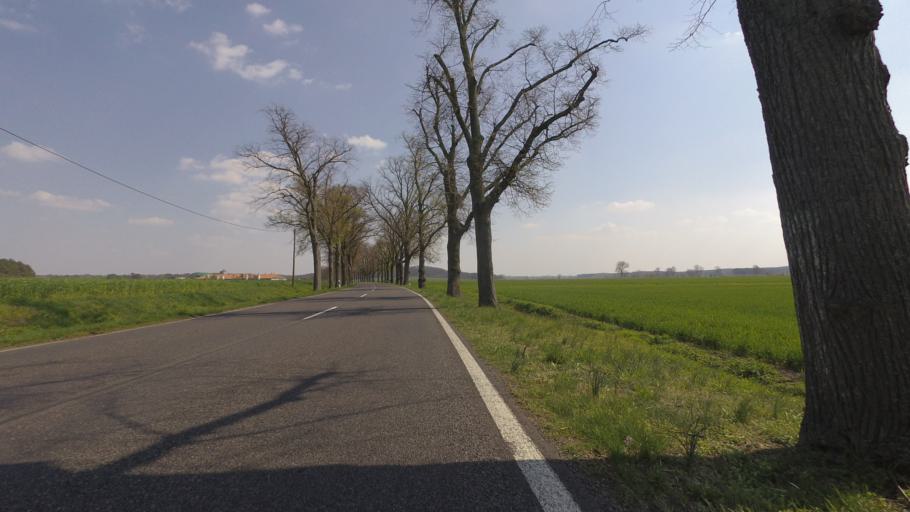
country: DE
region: Brandenburg
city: Mittenwalde
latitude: 52.2713
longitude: 13.4824
